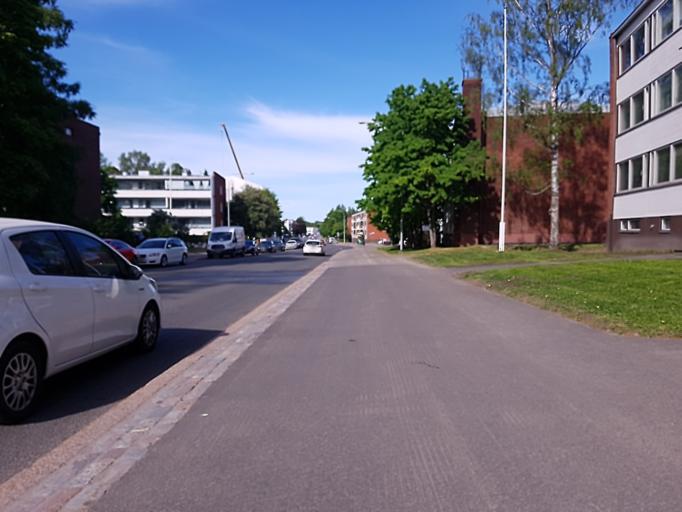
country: FI
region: Uusimaa
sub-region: Helsinki
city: Helsinki
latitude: 60.2237
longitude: 24.9502
